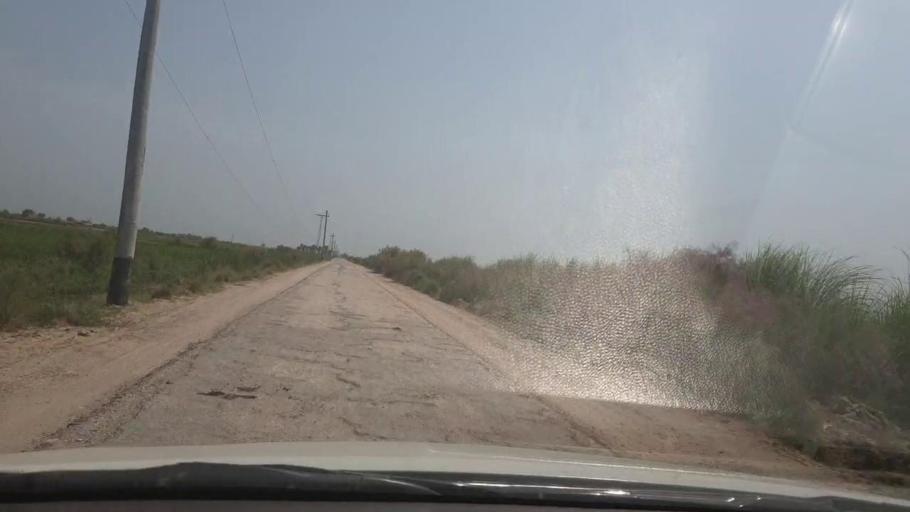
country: PK
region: Sindh
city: Garhi Yasin
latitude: 27.9650
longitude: 68.5043
